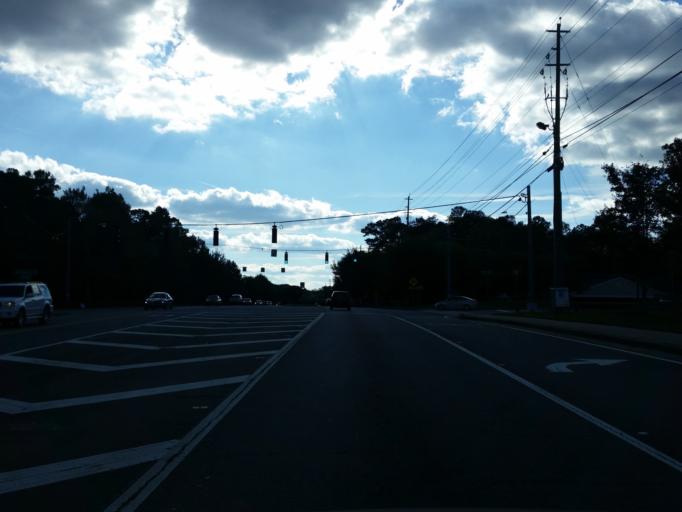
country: US
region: Georgia
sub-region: Cobb County
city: Marietta
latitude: 33.9514
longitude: -84.5823
